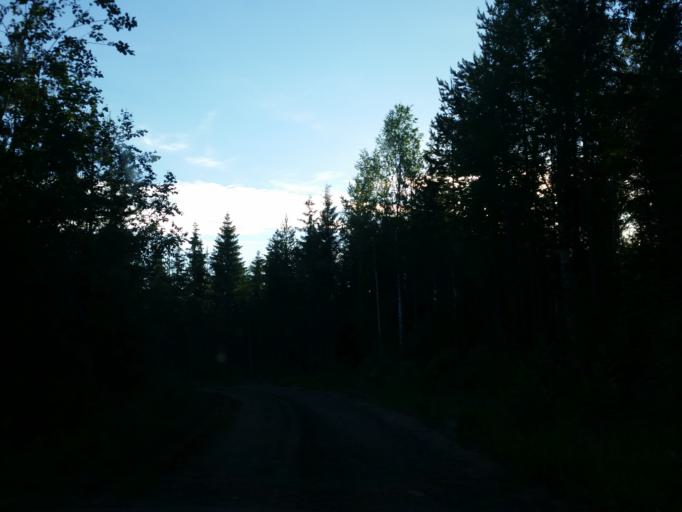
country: FI
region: Northern Savo
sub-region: Sisae-Savo
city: Tervo
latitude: 63.0572
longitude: 26.6363
